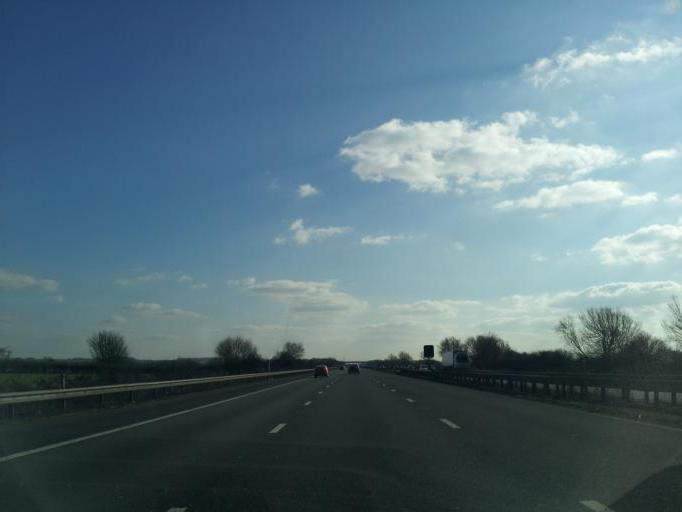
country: GB
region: England
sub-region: Somerset
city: Highbridge
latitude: 51.2056
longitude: -2.9663
